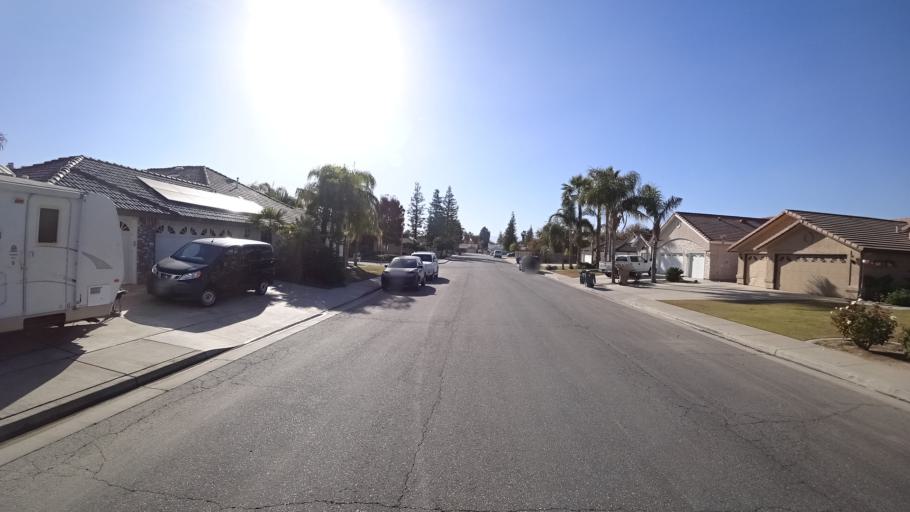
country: US
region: California
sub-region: Kern County
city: Greenfield
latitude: 35.2786
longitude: -119.0428
